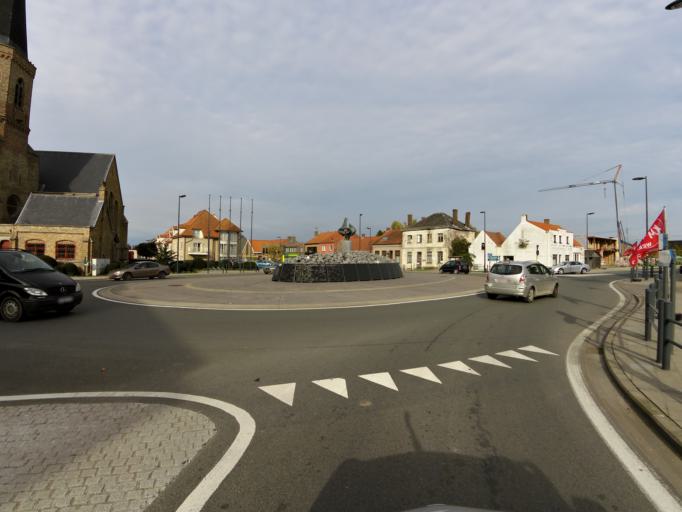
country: BE
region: Flanders
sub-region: Provincie West-Vlaanderen
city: Oudenburg
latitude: 51.1644
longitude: 3.0155
